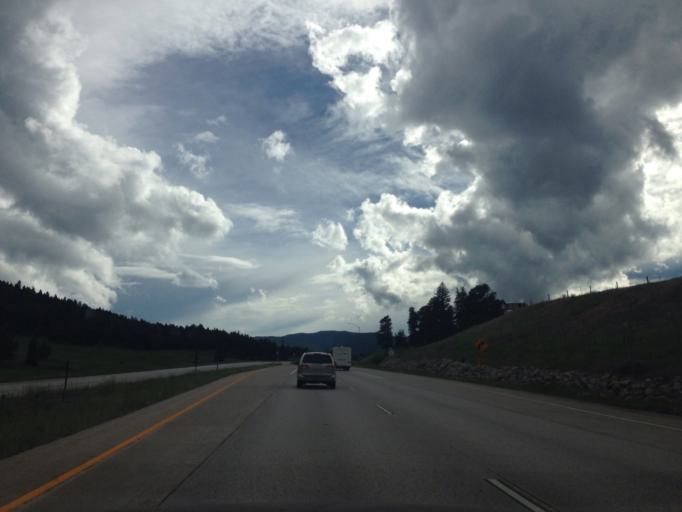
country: US
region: Colorado
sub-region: Jefferson County
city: Indian Hills
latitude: 39.5449
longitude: -105.2807
